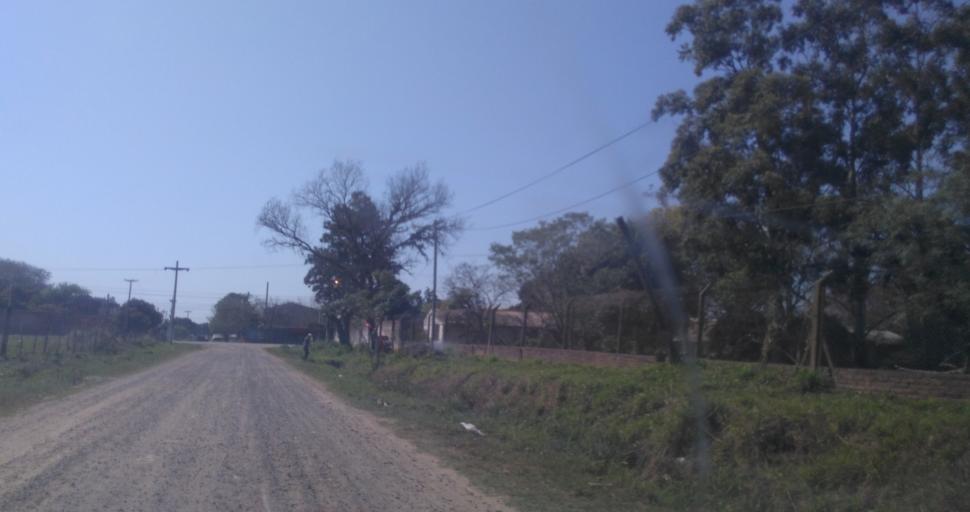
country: AR
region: Chaco
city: Fontana
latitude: -27.4287
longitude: -59.0279
